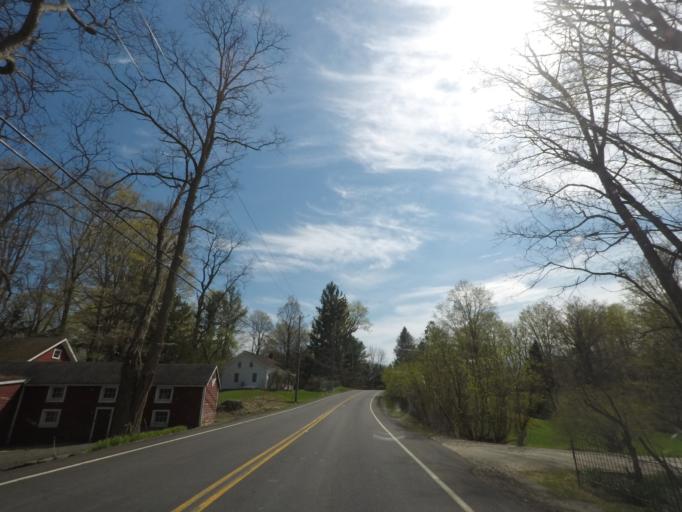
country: US
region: New York
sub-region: Columbia County
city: Chatham
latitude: 42.3942
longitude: -73.5269
